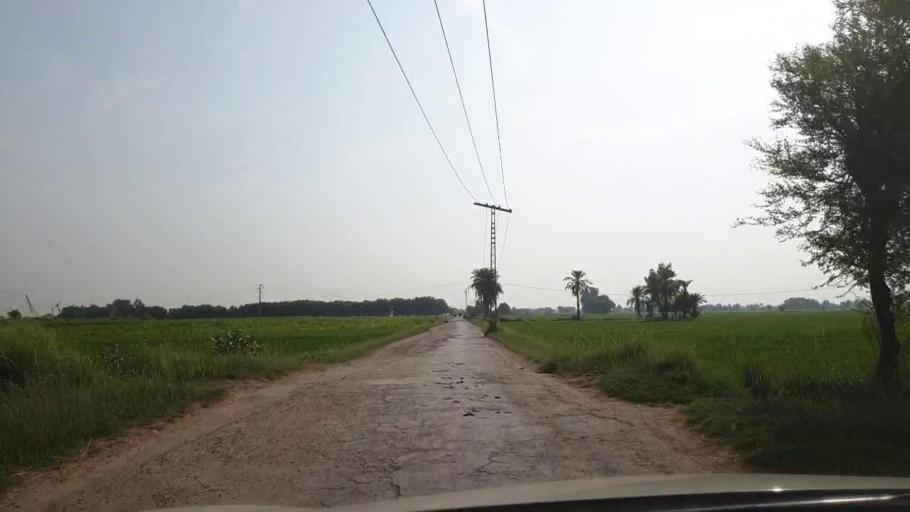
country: PK
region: Sindh
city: Larkana
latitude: 27.4491
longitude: 68.1870
